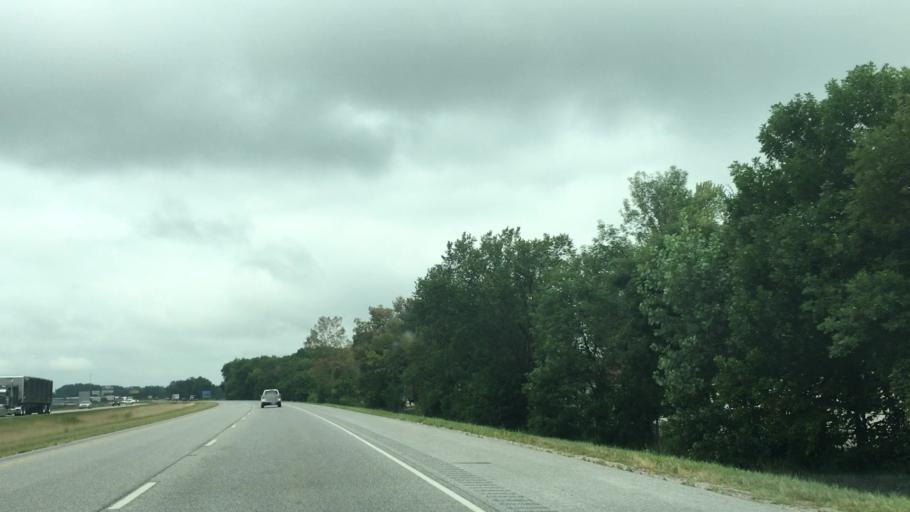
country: US
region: Illinois
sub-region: Rock Island County
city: Moline
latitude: 41.4581
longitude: -90.5116
